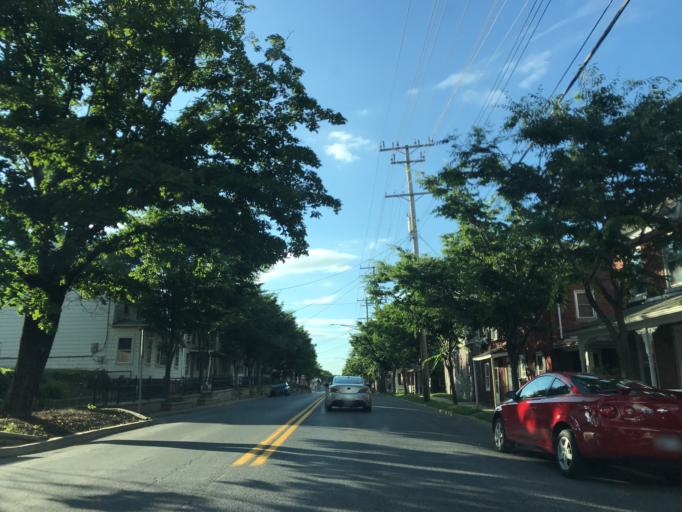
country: US
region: Maryland
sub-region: Carroll County
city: Manchester
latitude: 39.6583
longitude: -76.8832
